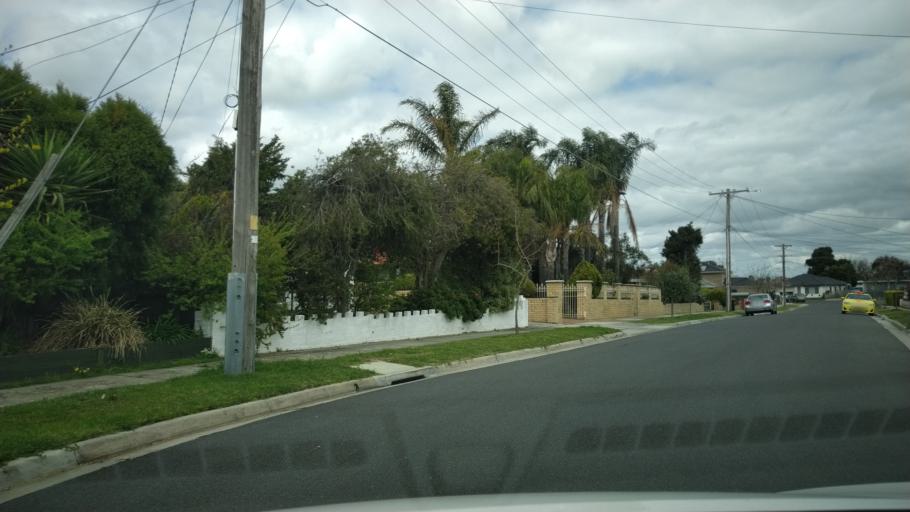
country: AU
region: Victoria
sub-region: Greater Dandenong
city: Noble Park
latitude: -37.9692
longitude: 145.1696
